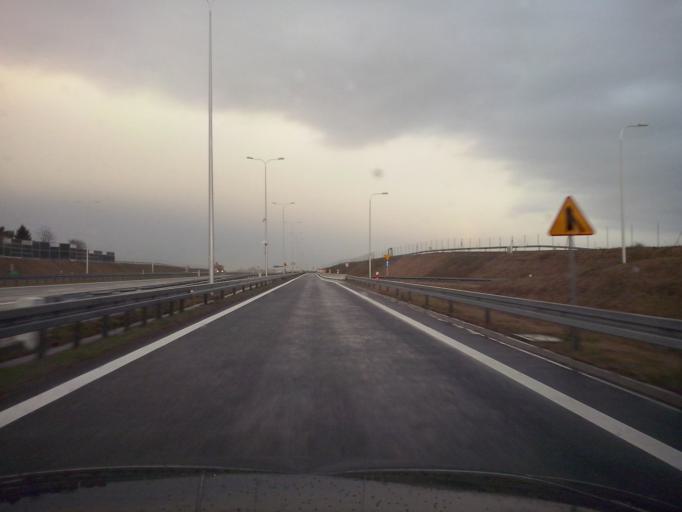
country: PL
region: Lublin Voivodeship
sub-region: Powiat lubelski
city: Jastkow
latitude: 51.2830
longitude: 22.4554
